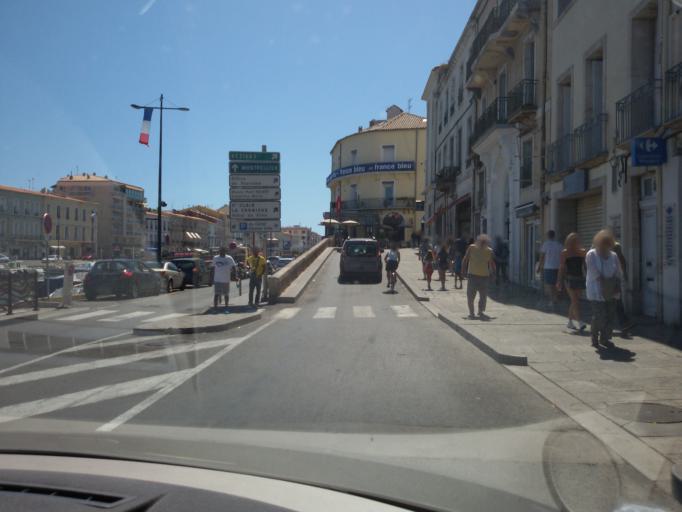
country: FR
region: Languedoc-Roussillon
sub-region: Departement de l'Herault
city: Sete
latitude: 43.4030
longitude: 3.6970
